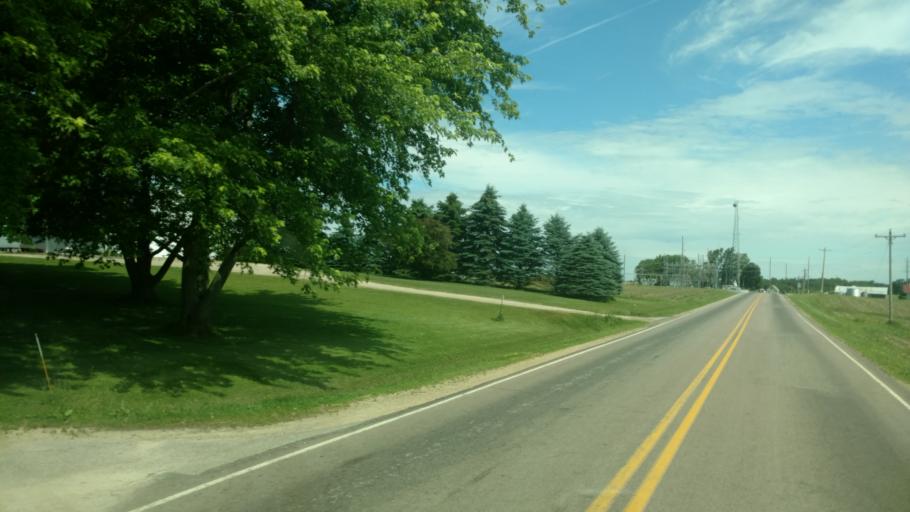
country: US
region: Wisconsin
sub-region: Vernon County
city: Hillsboro
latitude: 43.6640
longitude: -90.4587
